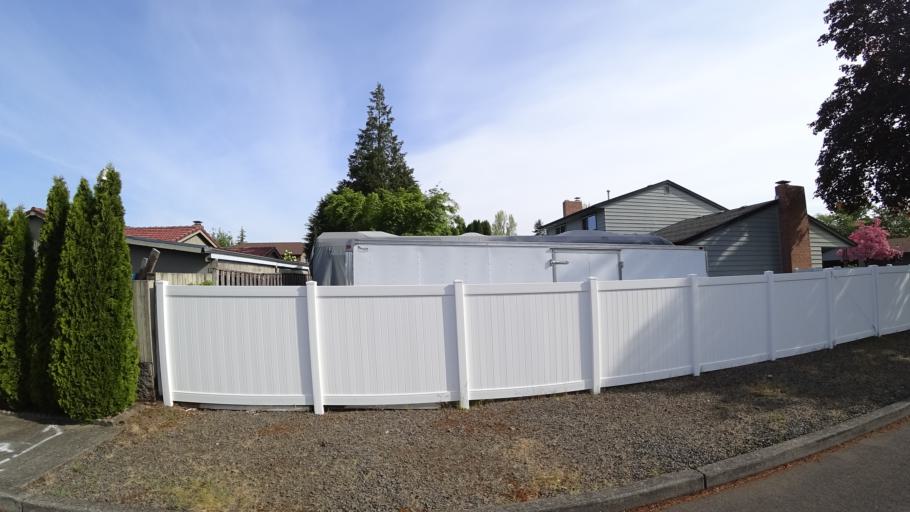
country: US
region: Oregon
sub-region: Washington County
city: Hillsboro
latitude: 45.5261
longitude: -122.9652
